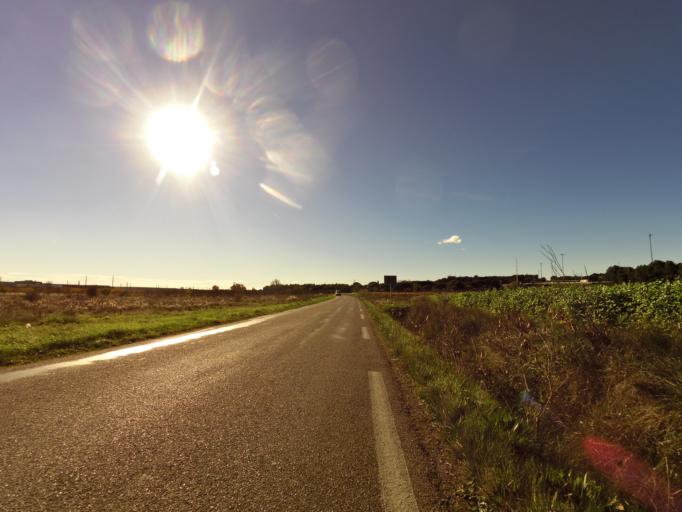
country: FR
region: Languedoc-Roussillon
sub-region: Departement du Gard
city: Aigues-Vives
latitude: 43.7265
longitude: 4.1879
